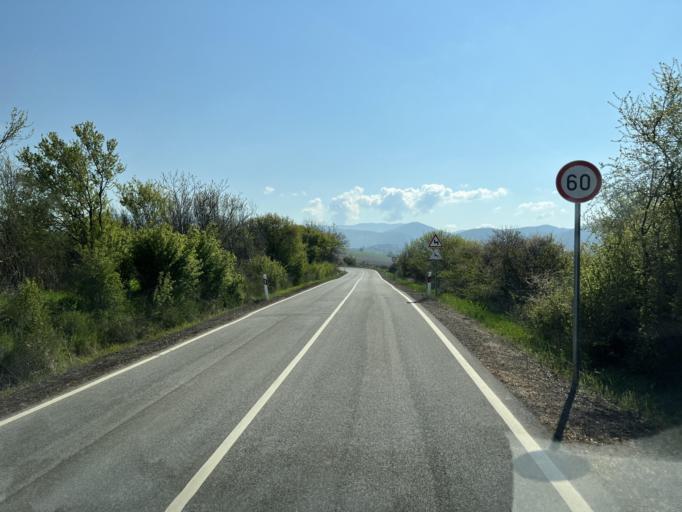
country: HU
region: Pest
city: Szob
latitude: 47.9372
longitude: 18.7933
